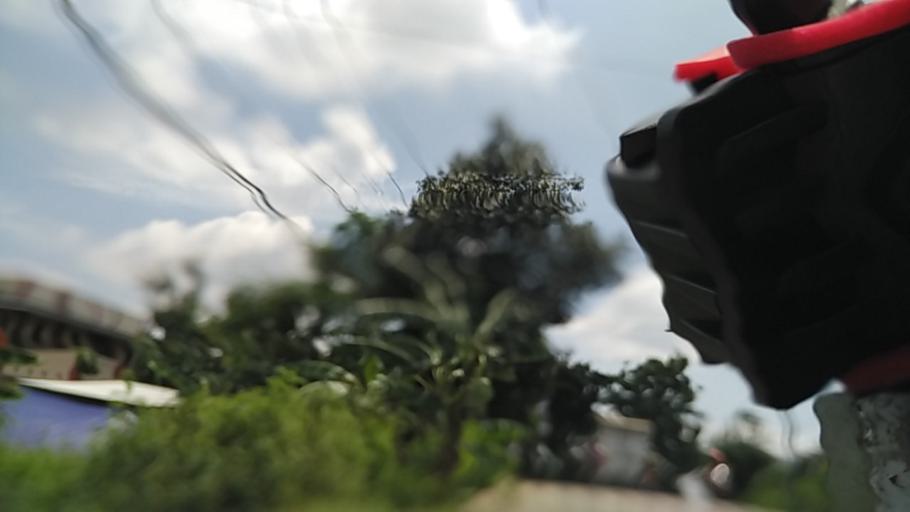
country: ID
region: Central Java
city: Semarang
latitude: -7.0131
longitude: 110.3714
